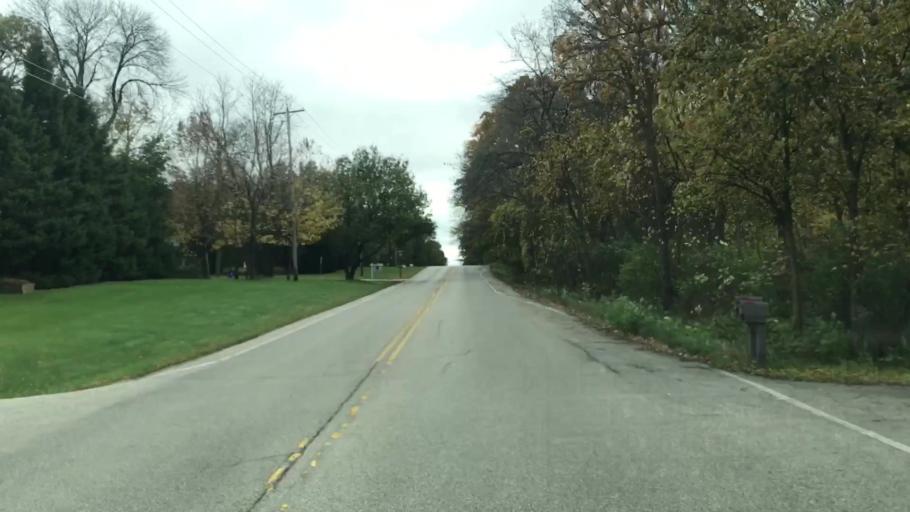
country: US
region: Wisconsin
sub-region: Waukesha County
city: Brookfield
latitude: 43.0605
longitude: -88.1020
